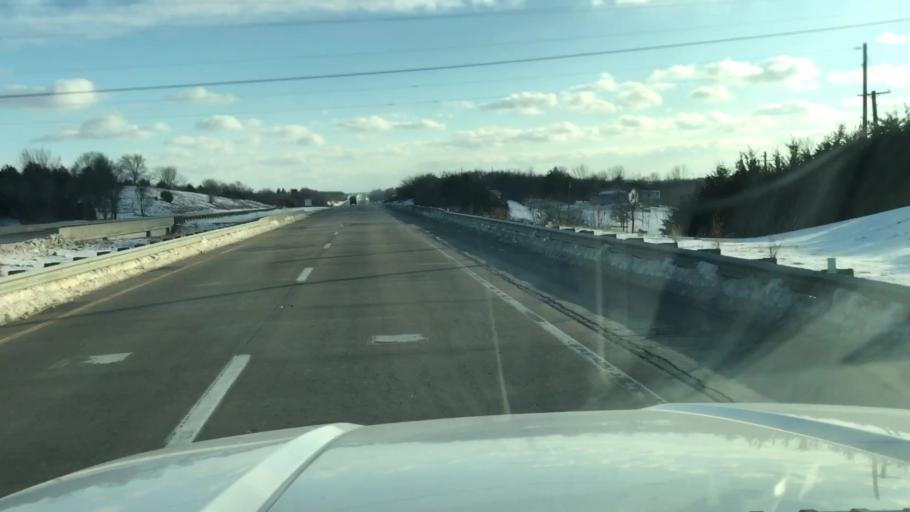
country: US
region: Missouri
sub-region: Andrew County
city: Savannah
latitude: 39.9488
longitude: -94.8603
